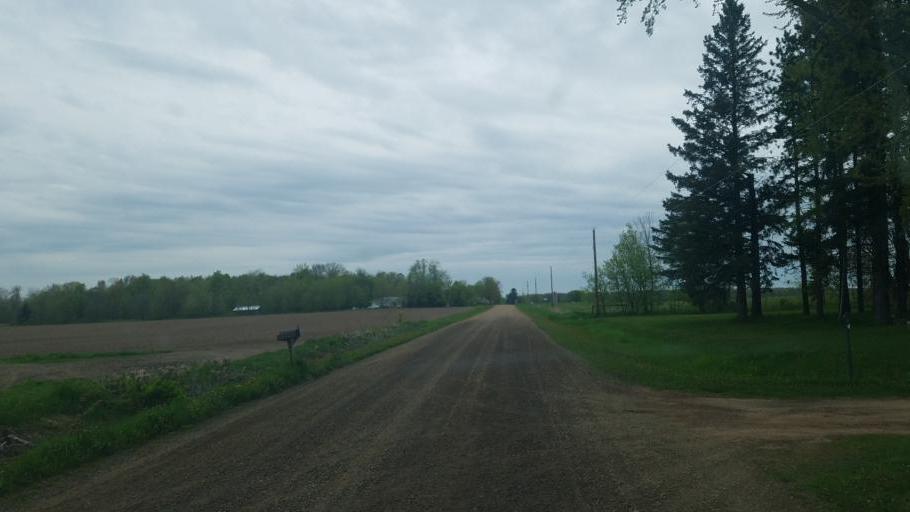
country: US
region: Wisconsin
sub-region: Clark County
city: Loyal
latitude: 44.6320
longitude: -90.4174
